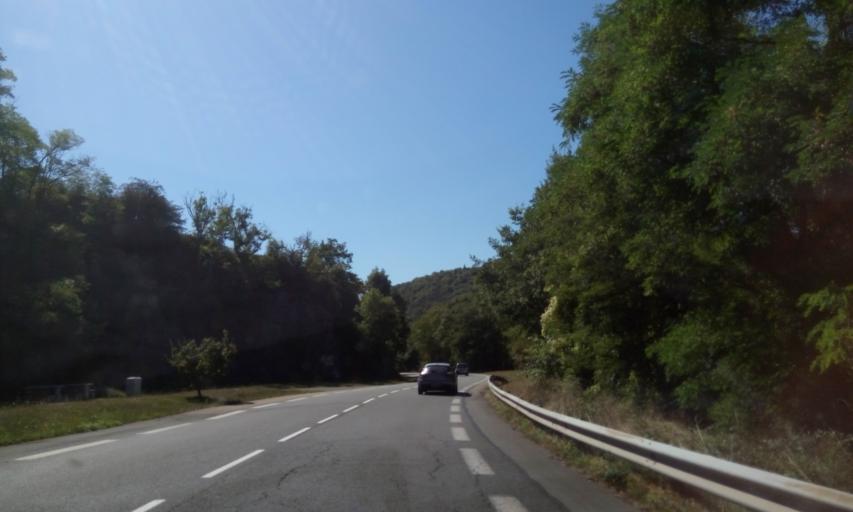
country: FR
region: Rhone-Alpes
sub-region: Departement du Rhone
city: Saint-Verand
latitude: 45.9696
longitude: 4.5094
